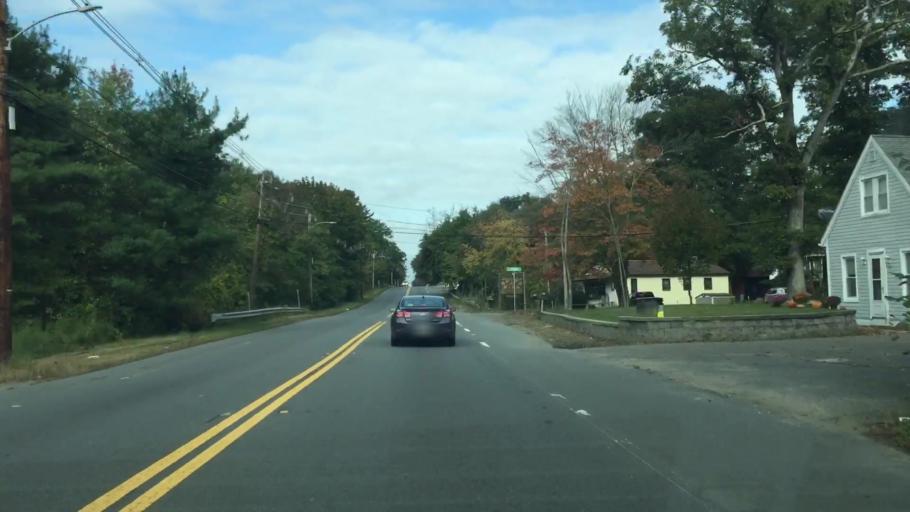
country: US
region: Massachusetts
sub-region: Essex County
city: Middleton
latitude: 42.6194
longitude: -71.0506
